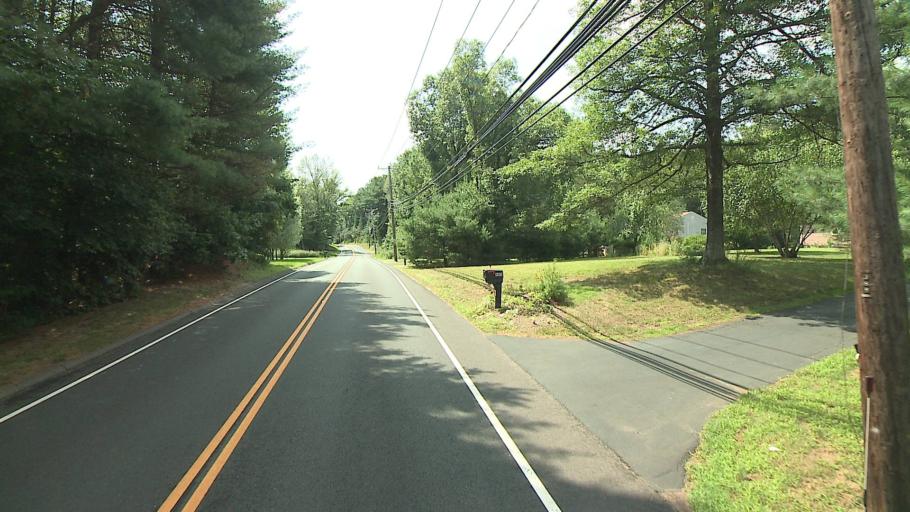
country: US
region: Connecticut
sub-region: Hartford County
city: Collinsville
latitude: 41.7858
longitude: -72.8928
